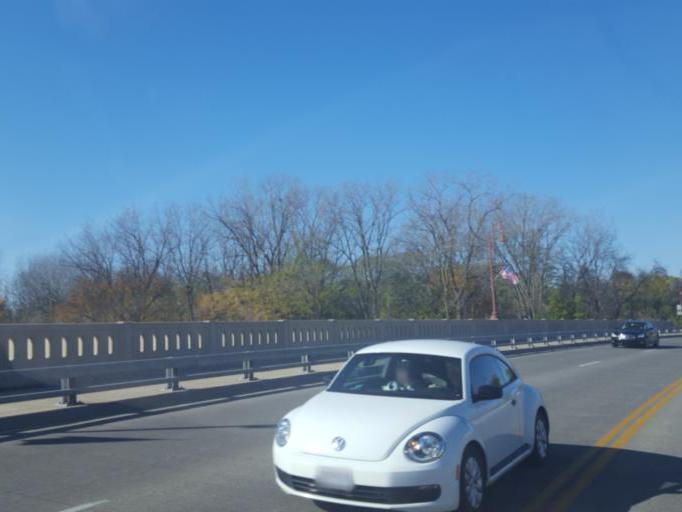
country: US
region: Ohio
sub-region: Lucas County
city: Maumee
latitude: 41.5576
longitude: -83.6510
